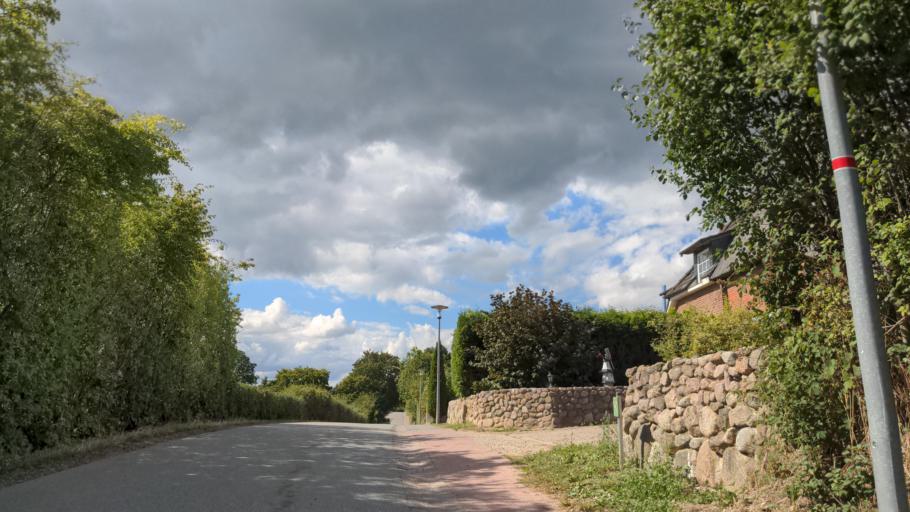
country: DE
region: Schleswig-Holstein
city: Kasseedorf
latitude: 54.1656
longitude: 10.7165
